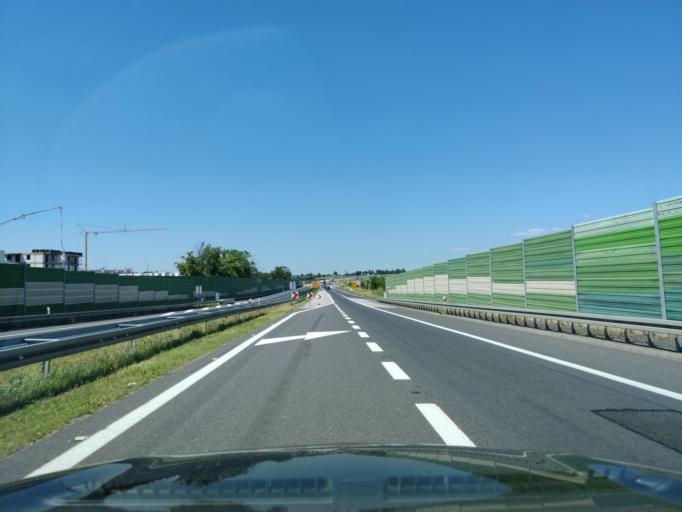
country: PL
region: Masovian Voivodeship
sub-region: Powiat plonski
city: Plonsk
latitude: 52.6329
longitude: 20.3809
